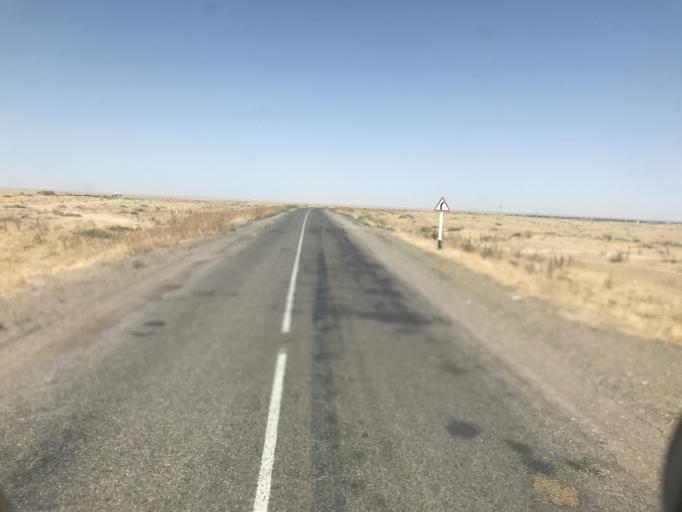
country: UZ
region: Toshkent
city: Chinoz
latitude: 41.1762
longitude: 68.6343
